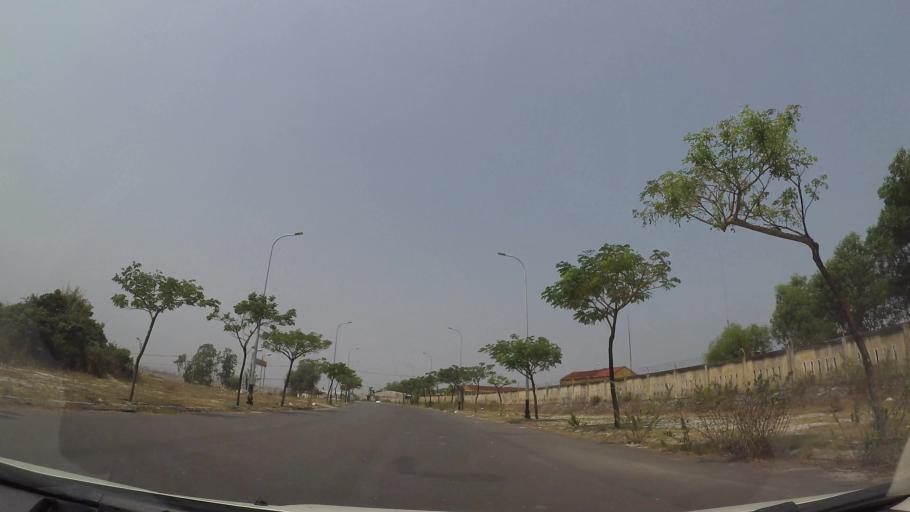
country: VN
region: Da Nang
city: Ngu Hanh Son
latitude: 16.0064
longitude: 108.2547
